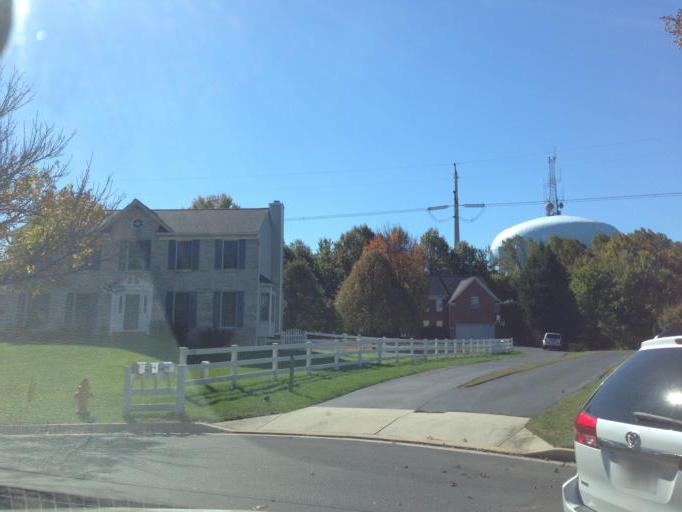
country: US
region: Maryland
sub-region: Howard County
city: Riverside
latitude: 39.1492
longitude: -76.8952
